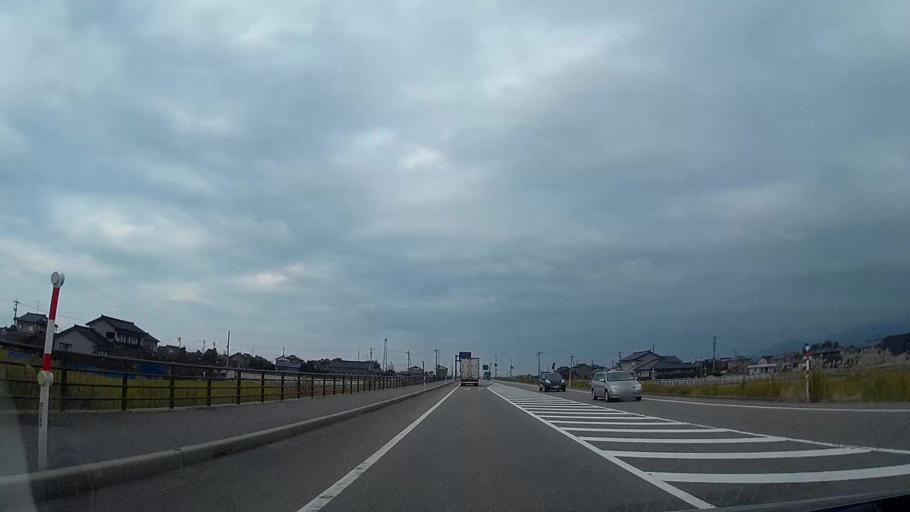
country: JP
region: Toyama
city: Nyuzen
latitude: 36.9193
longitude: 137.4651
